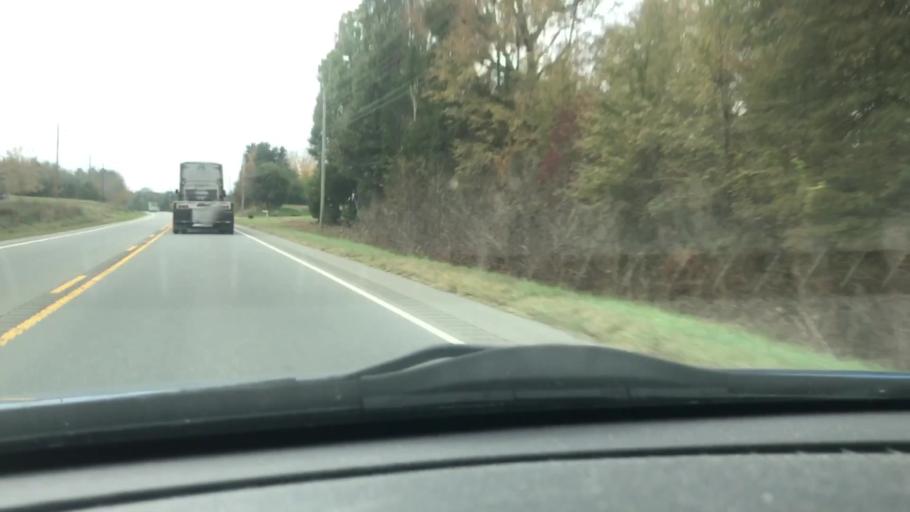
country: US
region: North Carolina
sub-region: Davidson County
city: Lexington
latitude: 35.8002
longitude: -80.1552
